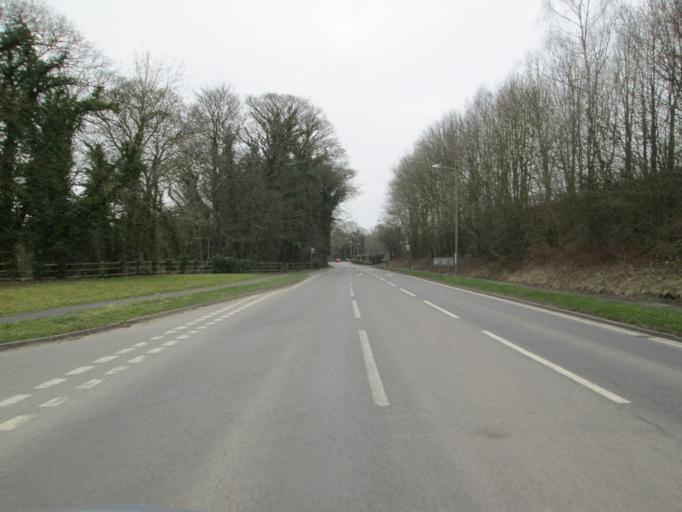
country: GB
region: England
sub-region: Derbyshire
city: Matlock
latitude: 53.1799
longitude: -1.6102
